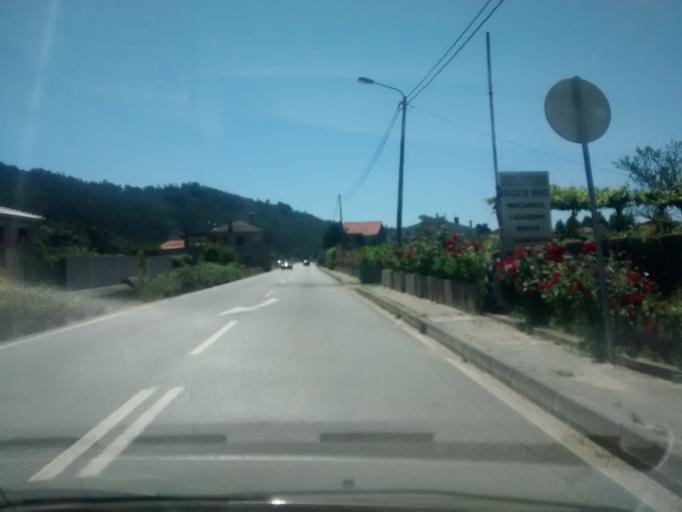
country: PT
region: Braga
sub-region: Barcelos
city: Galegos
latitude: 41.5310
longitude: -8.5269
